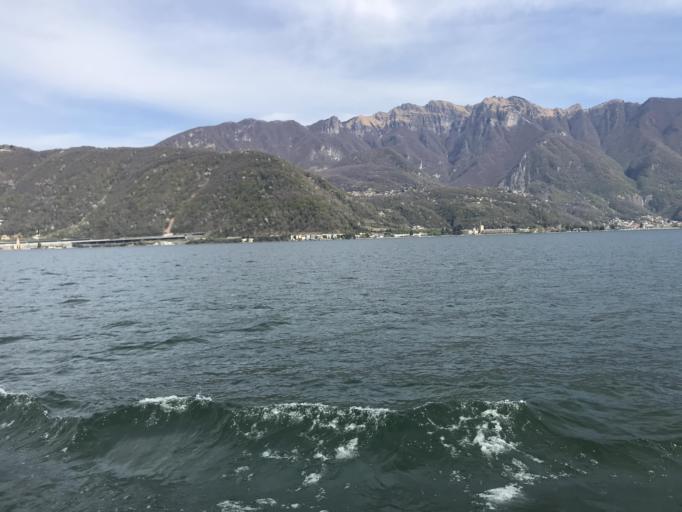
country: CH
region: Ticino
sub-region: Lugano District
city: Melide
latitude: 45.9396
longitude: 8.9435
